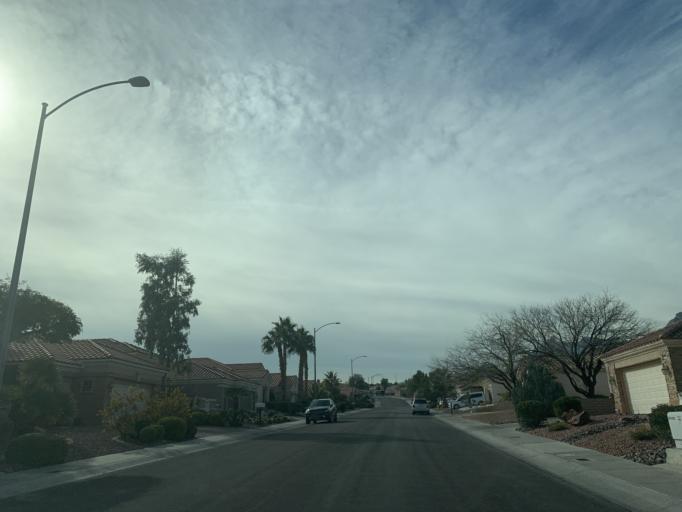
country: US
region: Nevada
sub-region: Clark County
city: Summerlin South
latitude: 36.2159
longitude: -115.3252
